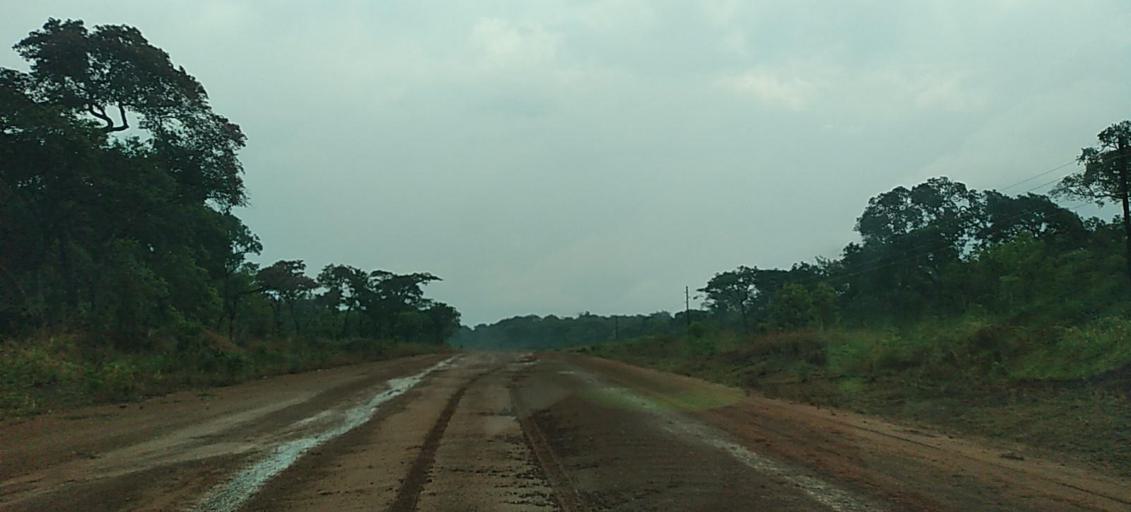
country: ZM
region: North-Western
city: Mwinilunga
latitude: -11.5848
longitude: 24.3883
